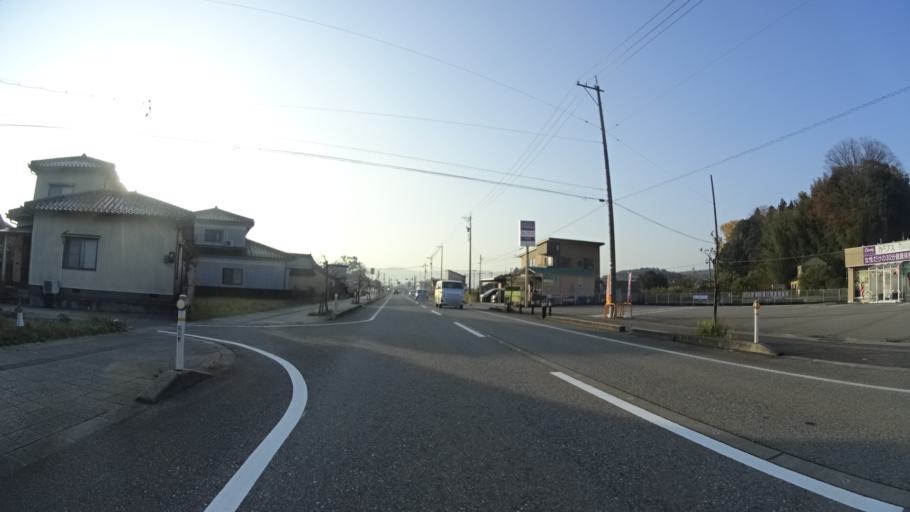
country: JP
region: Ishikawa
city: Nanao
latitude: 37.0501
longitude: 136.9566
